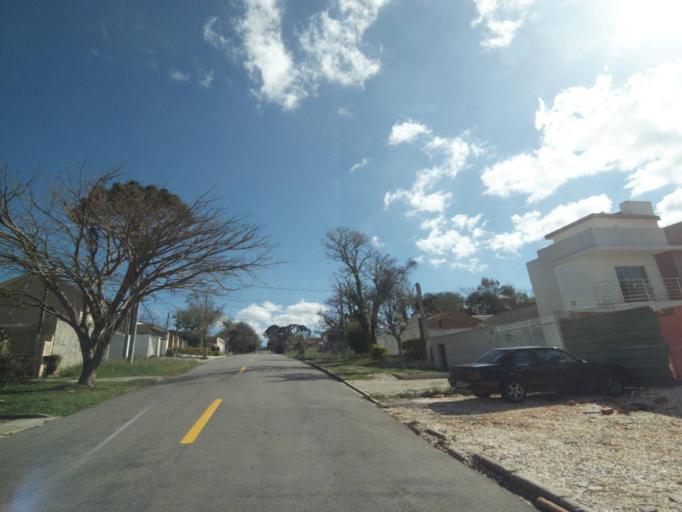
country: BR
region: Parana
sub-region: Curitiba
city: Curitiba
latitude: -25.3804
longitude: -49.2530
